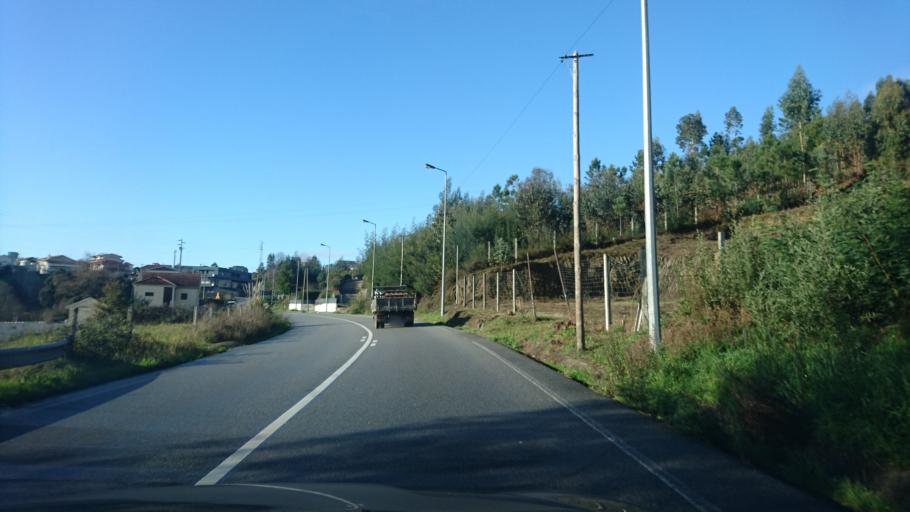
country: PT
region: Porto
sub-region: Paredes
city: Recarei
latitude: 41.1500
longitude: -8.3980
